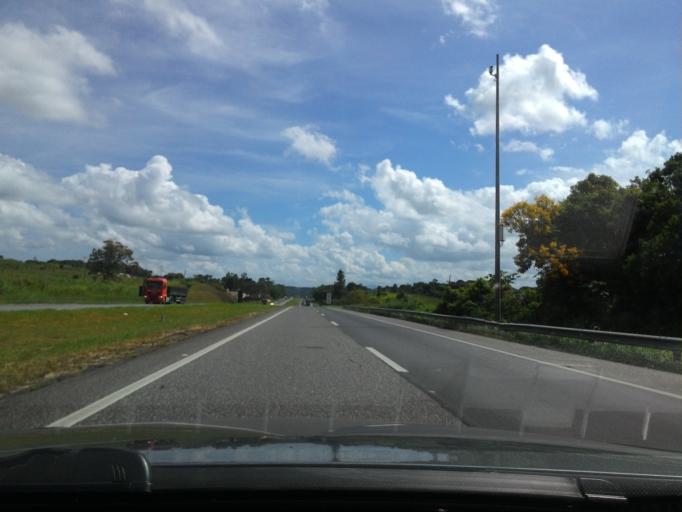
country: BR
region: Sao Paulo
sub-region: Pariquera-Acu
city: Pariquera Acu
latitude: -24.6344
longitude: -47.9083
